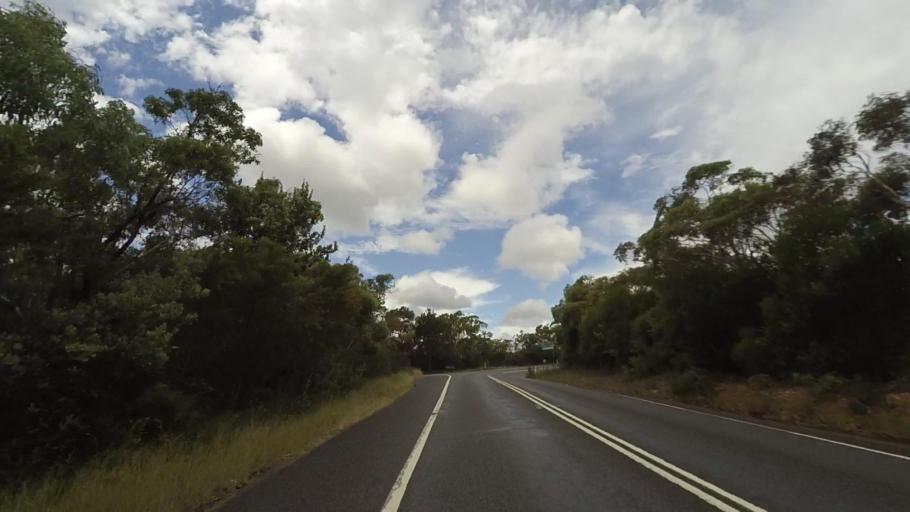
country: AU
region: New South Wales
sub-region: Sutherland Shire
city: Grays Point
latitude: -34.0858
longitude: 151.0690
